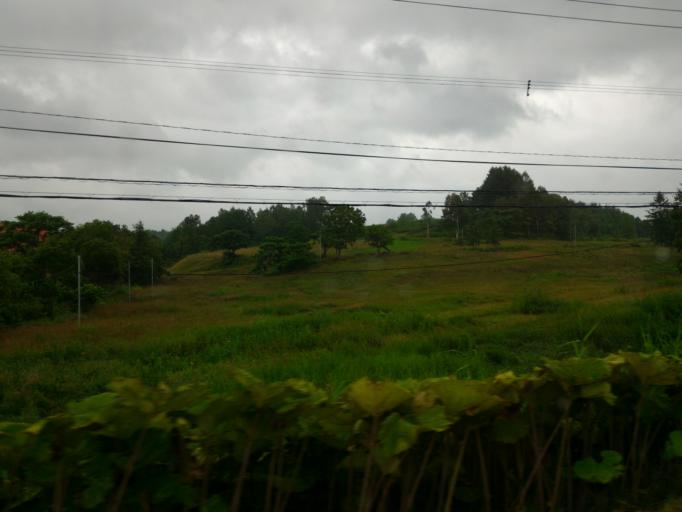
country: JP
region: Hokkaido
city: Nayoro
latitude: 44.6690
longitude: 142.2689
